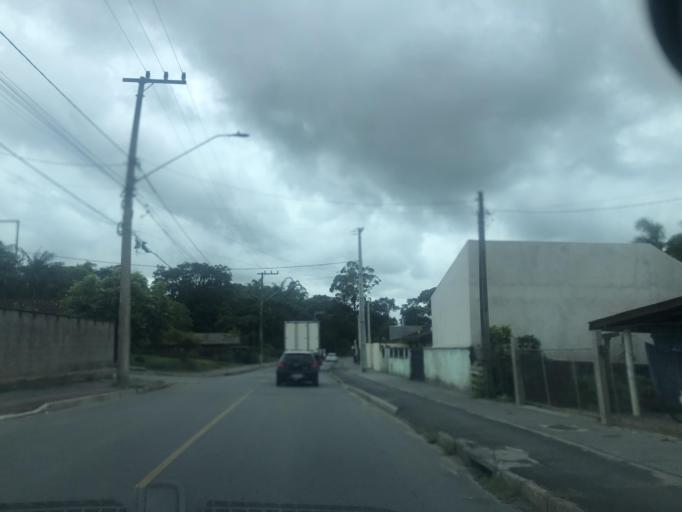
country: BR
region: Santa Catarina
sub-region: Joinville
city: Joinville
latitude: -26.3697
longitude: -48.7175
